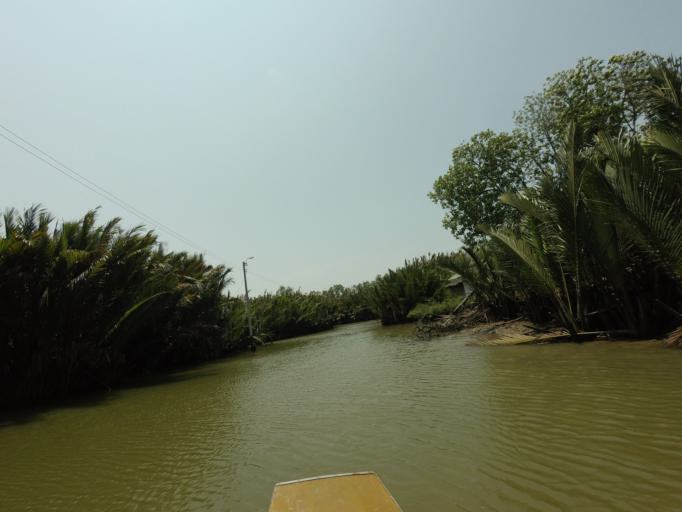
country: TH
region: Bangkok
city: Thung Khru
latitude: 13.5465
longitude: 100.4909
